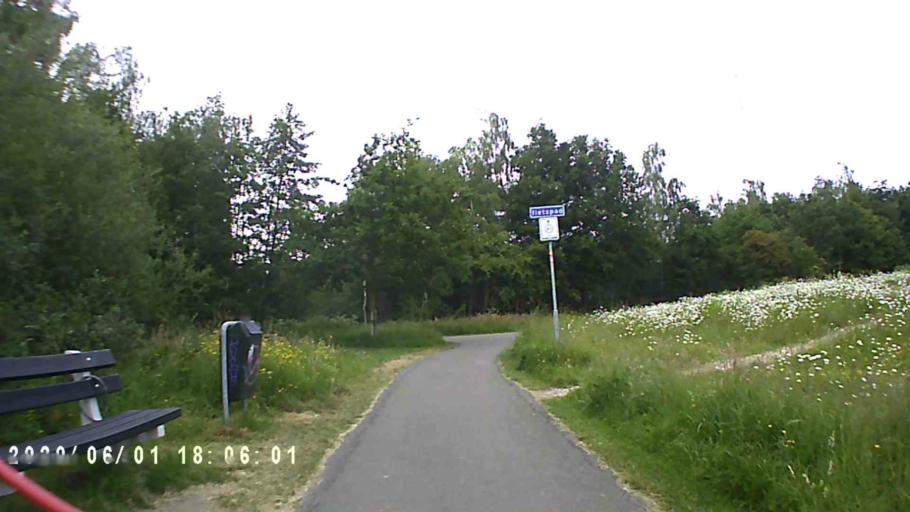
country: NL
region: Friesland
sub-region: Gemeente Tytsjerksteradiel
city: Sumar
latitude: 53.1790
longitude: 5.9945
